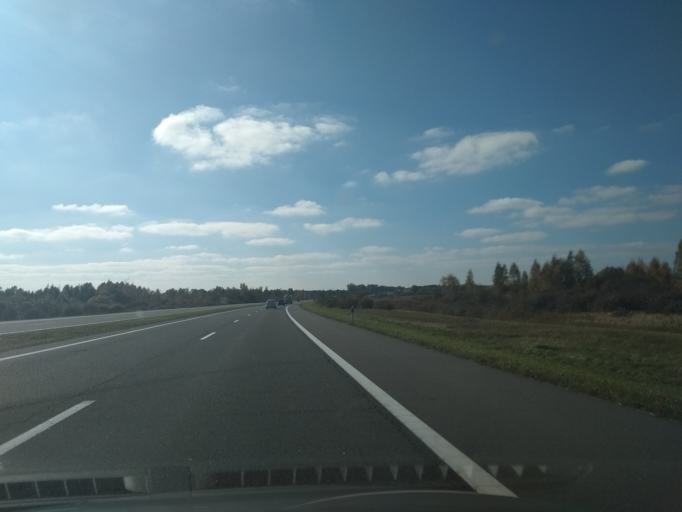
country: BY
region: Brest
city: Baranovichi
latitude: 53.1506
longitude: 25.9697
